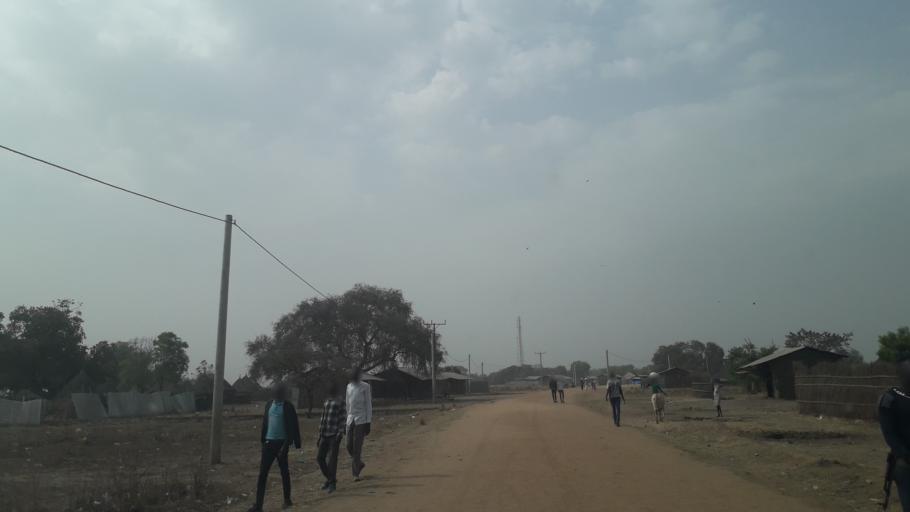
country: ET
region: Gambela
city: Gambela
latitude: 8.3059
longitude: 33.6865
